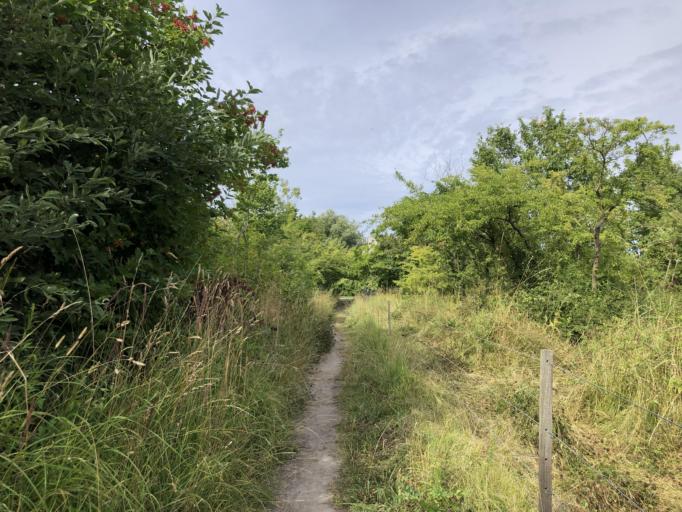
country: DK
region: Capital Region
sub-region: Kobenhavn
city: Christianshavn
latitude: 55.6586
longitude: 12.5813
